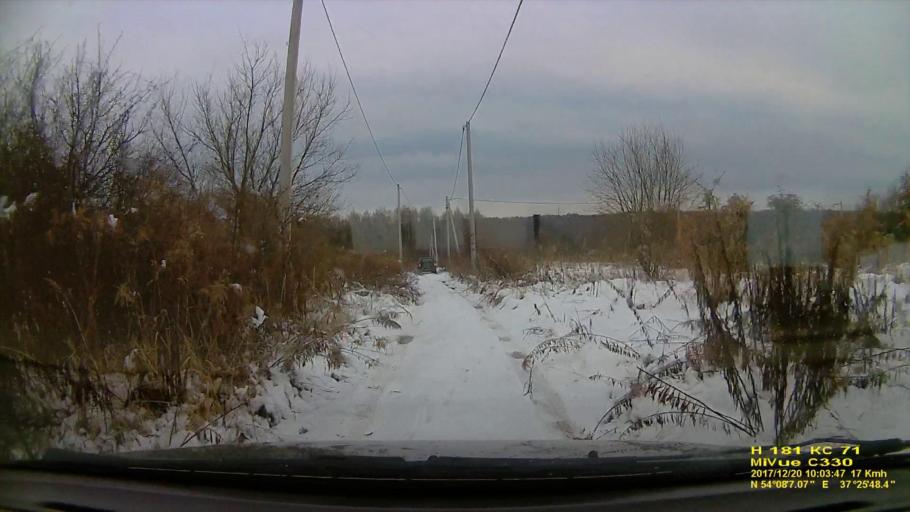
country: RU
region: Tula
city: Kosaya Gora
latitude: 54.1352
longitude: 37.4301
